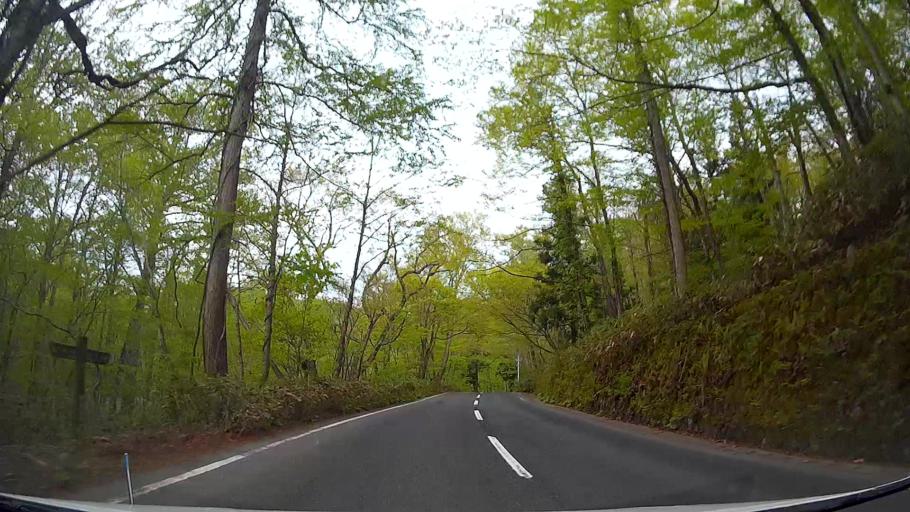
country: JP
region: Aomori
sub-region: Aomori Shi
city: Furudate
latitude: 40.5669
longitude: 140.9753
